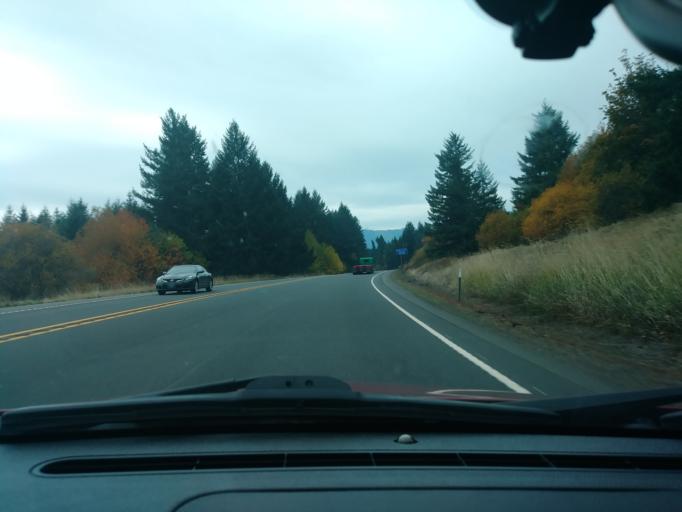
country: US
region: Oregon
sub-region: Washington County
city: Banks
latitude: 45.6200
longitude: -123.2111
